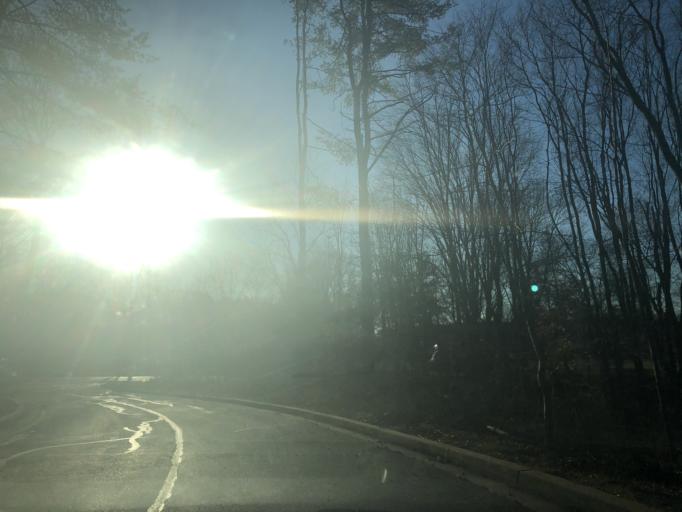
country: US
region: Maryland
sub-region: Howard County
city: Columbia
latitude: 39.2076
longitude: -76.8269
